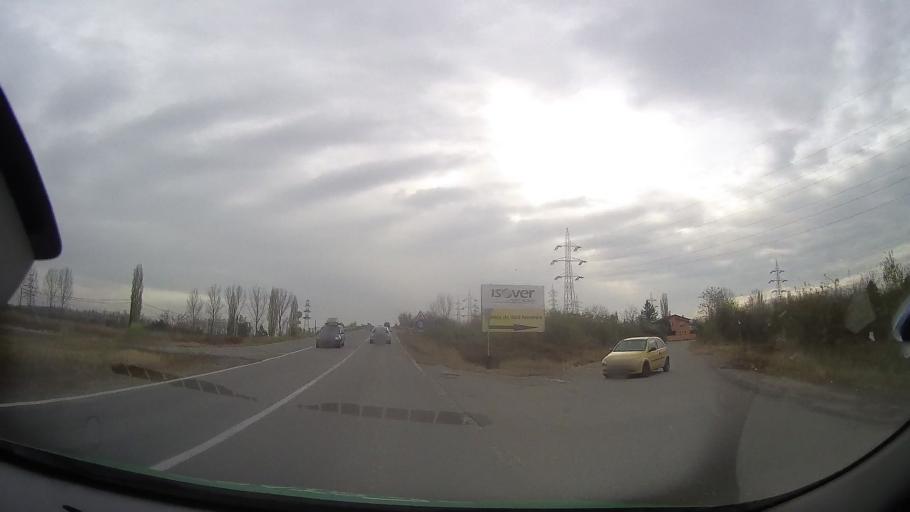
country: RO
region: Prahova
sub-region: Comuna Berceni
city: Berceni
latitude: 44.9427
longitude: 26.1011
